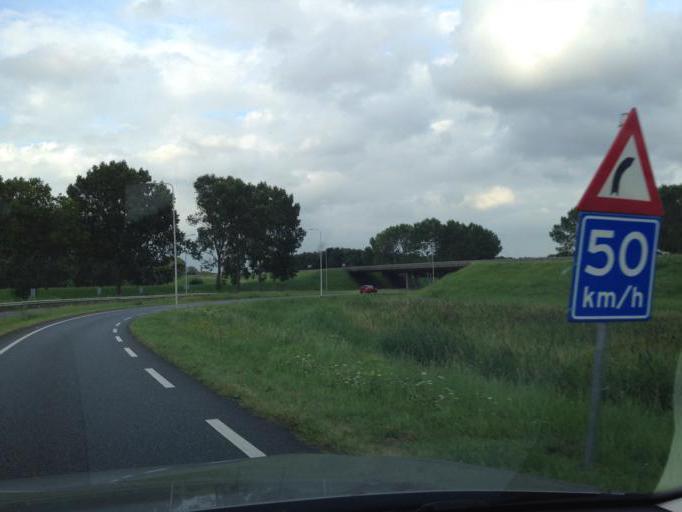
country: NL
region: Flevoland
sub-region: Gemeente Almere
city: Almere Stad
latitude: 52.3973
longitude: 5.2400
